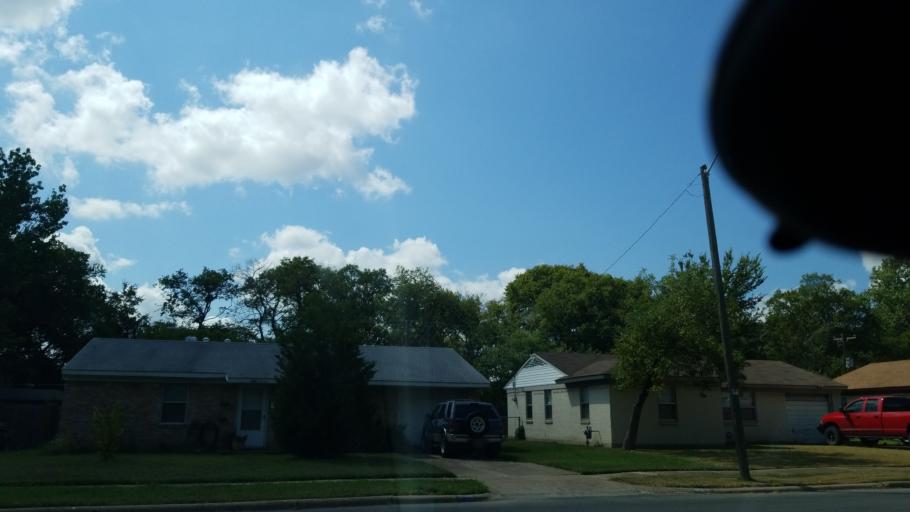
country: US
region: Texas
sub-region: Dallas County
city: Grand Prairie
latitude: 32.7167
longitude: -96.9971
